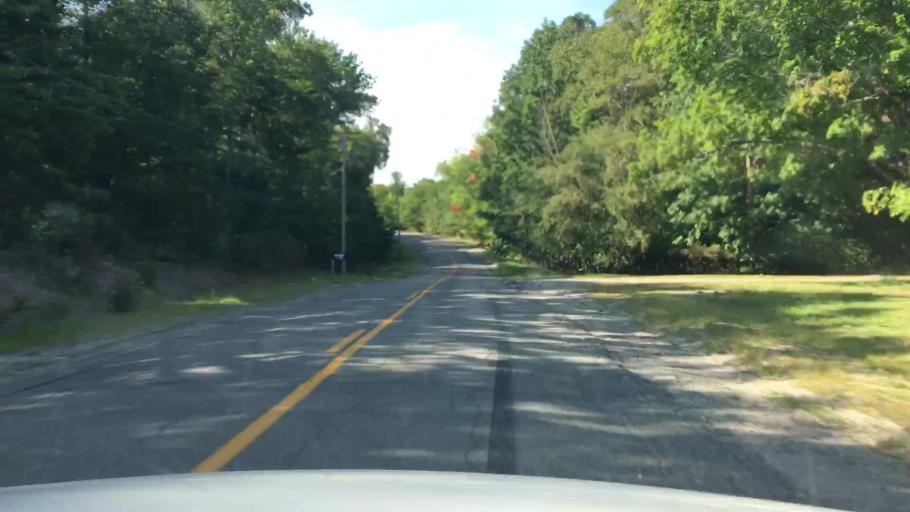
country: US
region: Maine
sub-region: Penobscot County
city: Enfield
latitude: 45.2233
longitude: -68.5381
